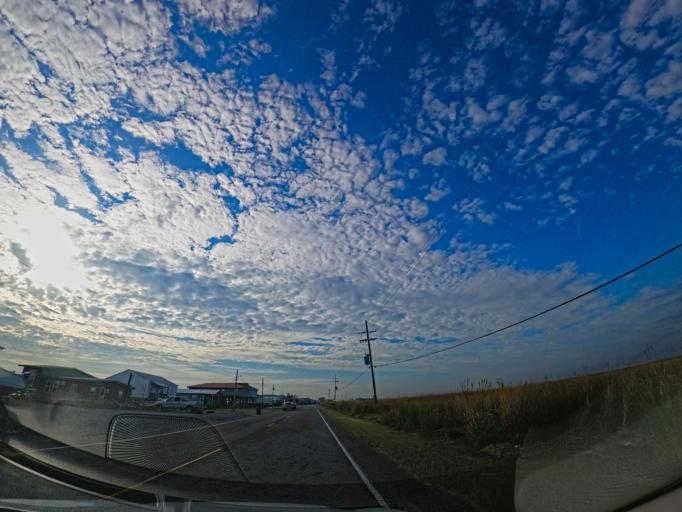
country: US
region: Louisiana
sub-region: Terrebonne Parish
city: Dulac
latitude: 29.2853
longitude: -90.6463
